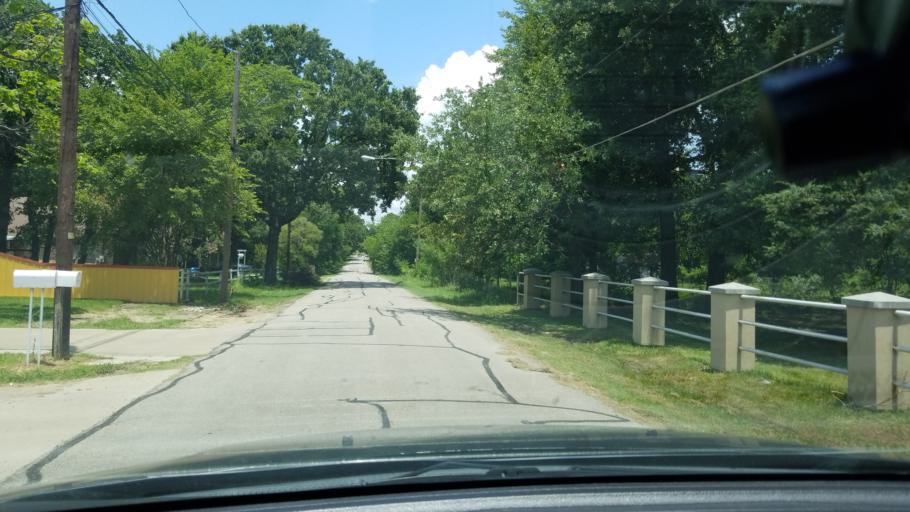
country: US
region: Texas
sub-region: Dallas County
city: Balch Springs
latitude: 32.7450
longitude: -96.6436
